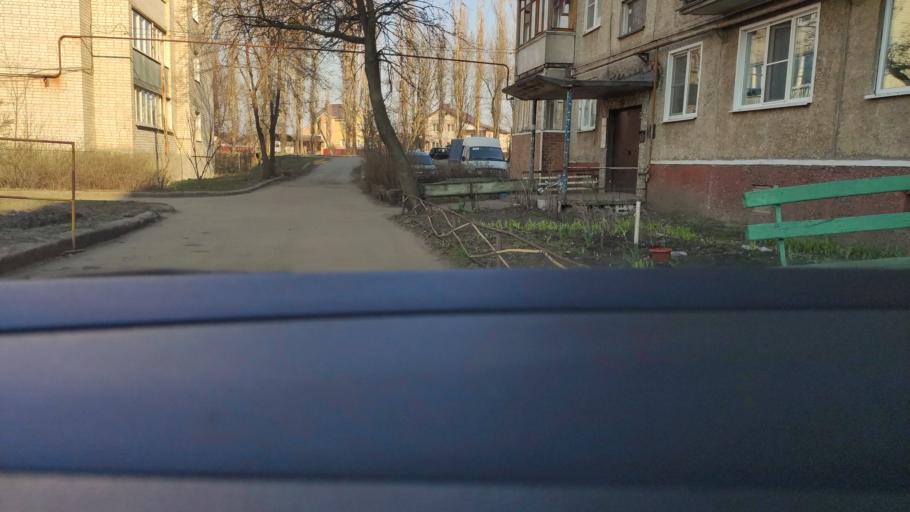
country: RU
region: Voronezj
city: Maslovka
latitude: 51.5872
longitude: 39.3210
